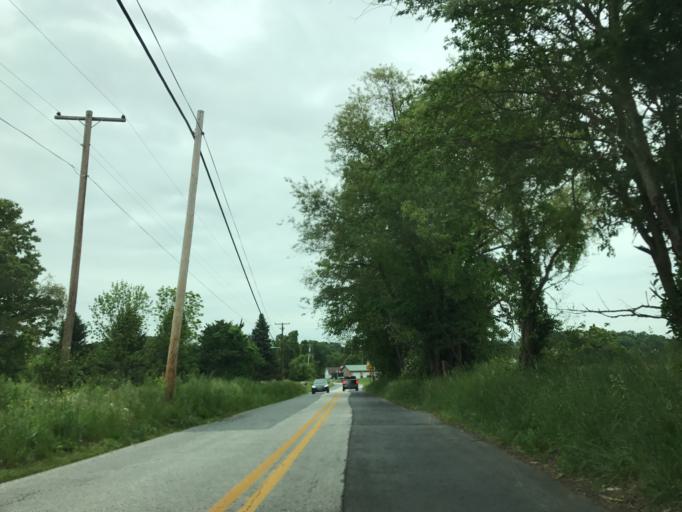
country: US
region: Maryland
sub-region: Carroll County
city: Hampstead
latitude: 39.6323
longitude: -76.8180
